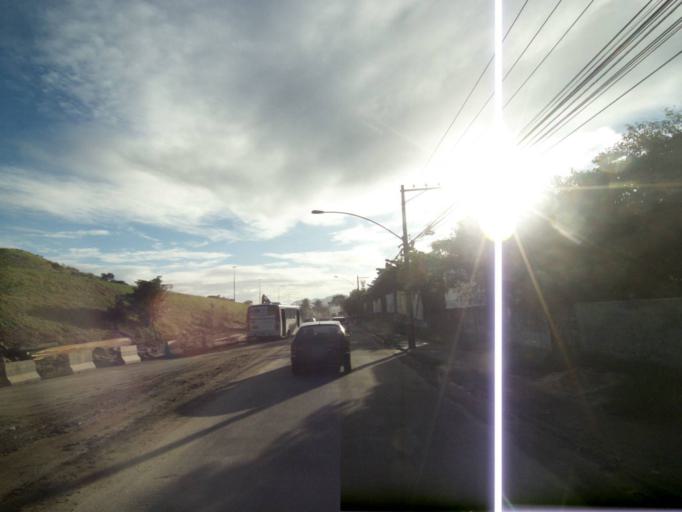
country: BR
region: Rio de Janeiro
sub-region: Nilopolis
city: Nilopolis
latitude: -22.8573
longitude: -43.4696
